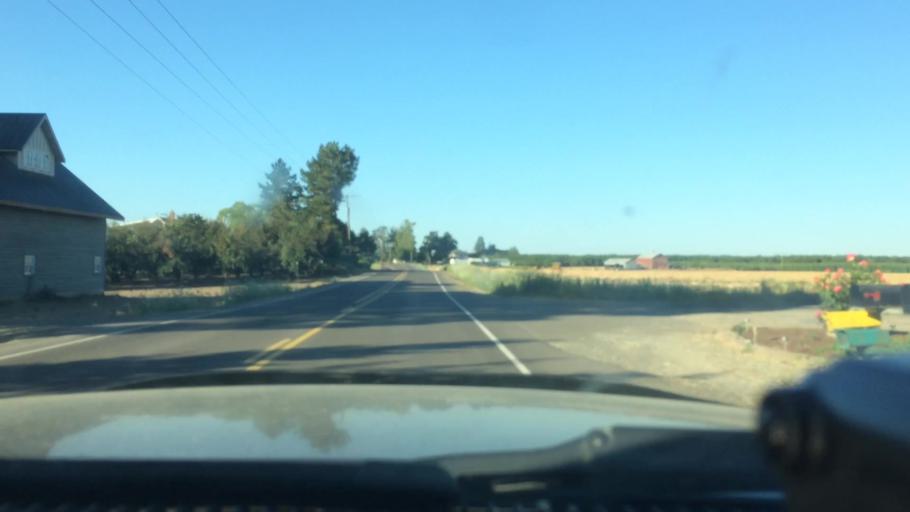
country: US
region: Oregon
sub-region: Yamhill County
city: Dundee
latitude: 45.2054
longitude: -122.9806
